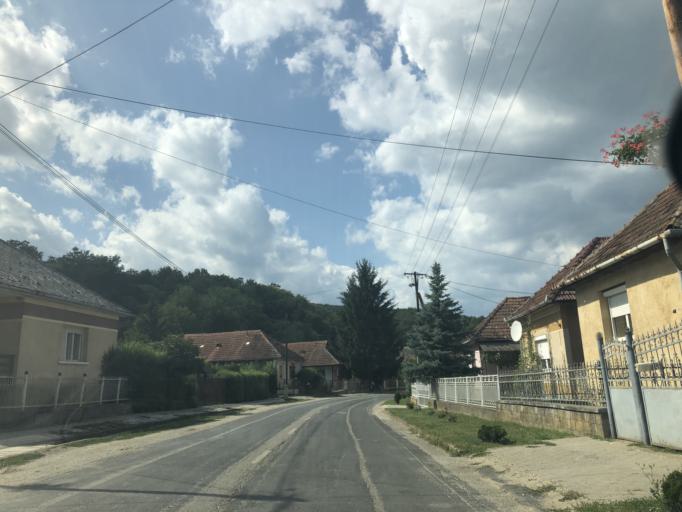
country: HU
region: Borsod-Abauj-Zemplen
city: Szendro
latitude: 48.4399
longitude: 20.7945
